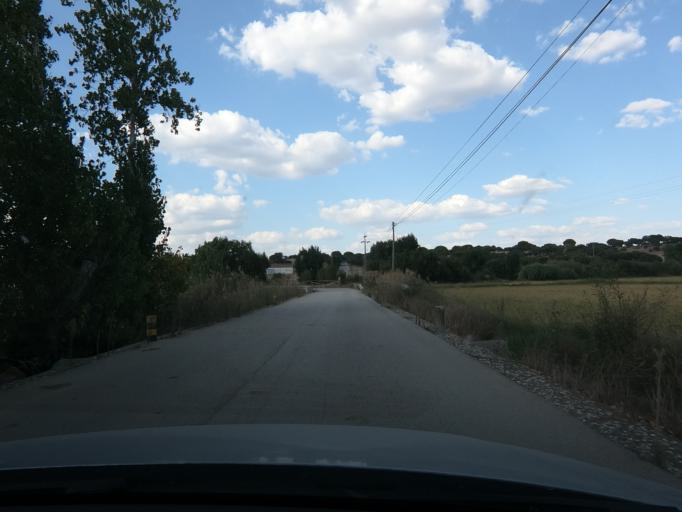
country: PT
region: Setubal
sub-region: Alcacer do Sal
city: Alcacer do Sal
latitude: 38.2503
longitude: -8.3586
